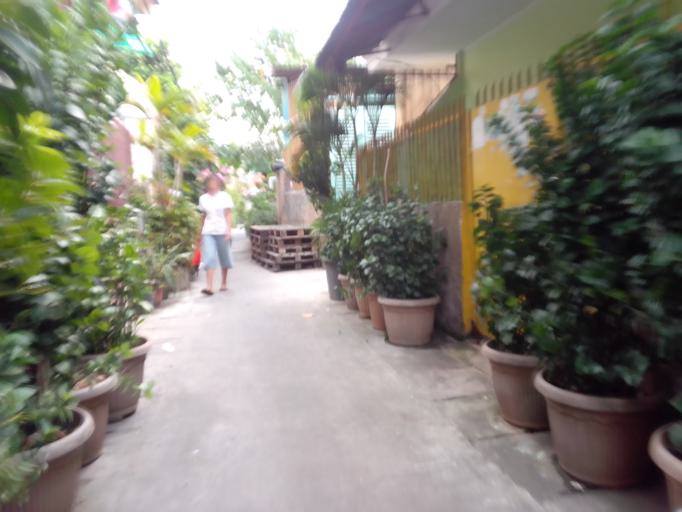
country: ID
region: Jakarta Raya
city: Jakarta
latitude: -6.1488
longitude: 106.8131
